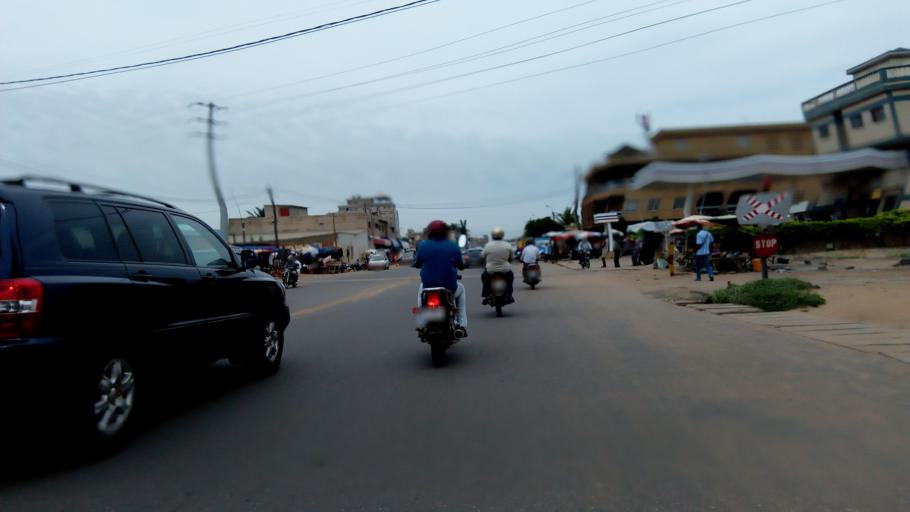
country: TG
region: Maritime
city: Lome
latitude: 6.1552
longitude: 1.2330
